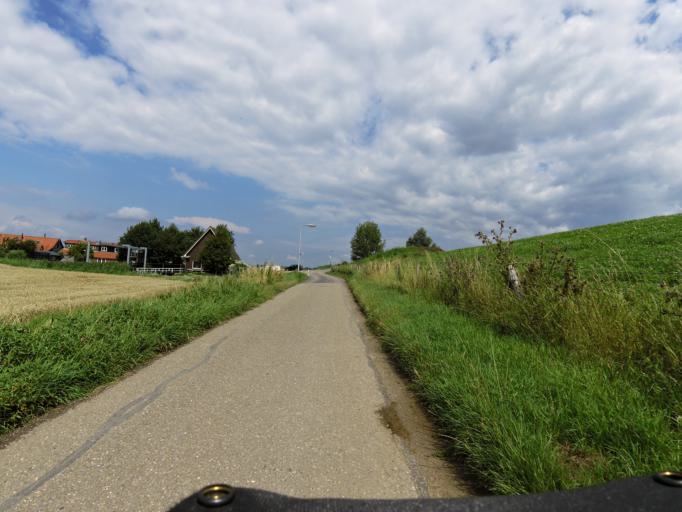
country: NL
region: South Holland
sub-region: Gemeente Strijen
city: Strijen
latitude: 51.7165
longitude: 4.5891
